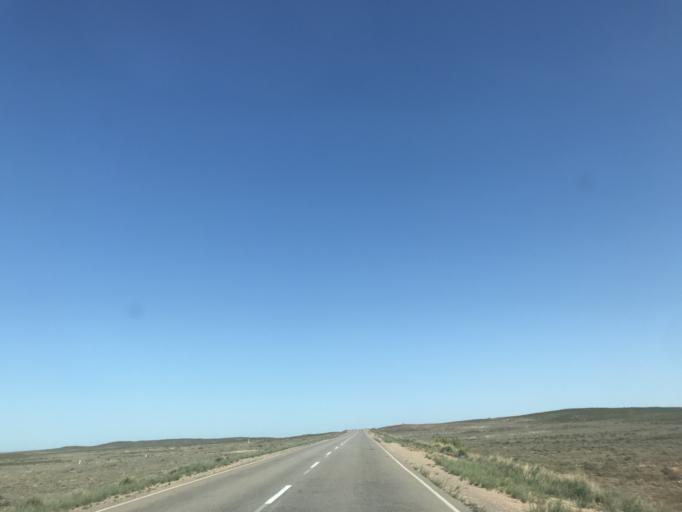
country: KZ
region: Zhambyl
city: Mynaral
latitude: 45.4930
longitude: 73.5258
